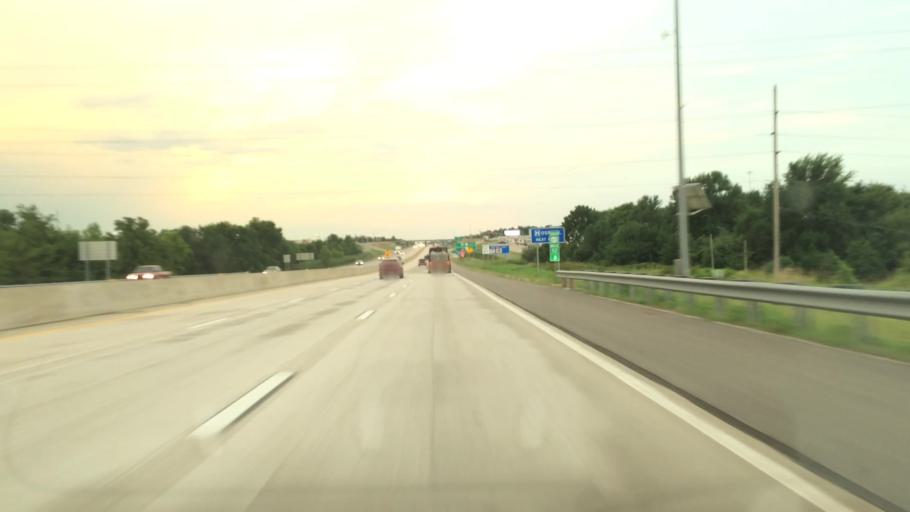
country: US
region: Missouri
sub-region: Greene County
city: Springfield
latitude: 37.2321
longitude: -93.2251
